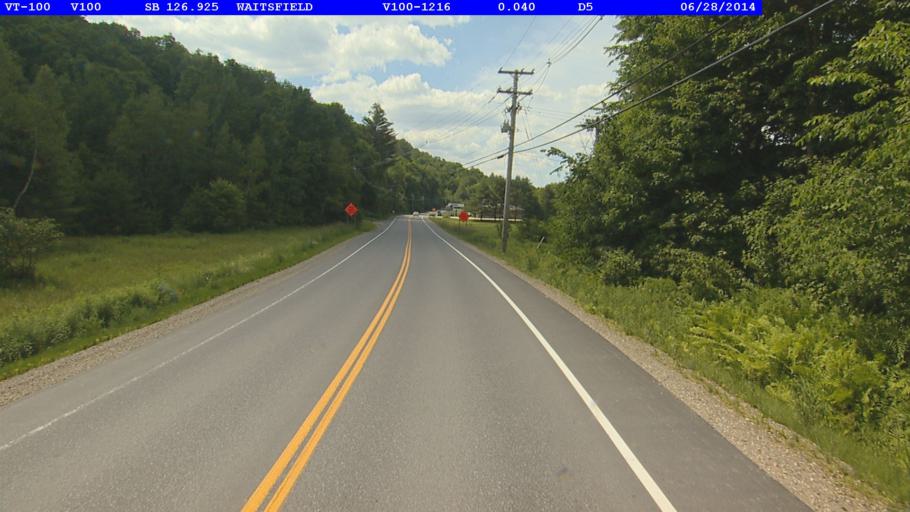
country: US
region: Vermont
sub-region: Washington County
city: Northfield
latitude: 44.1472
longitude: -72.8407
